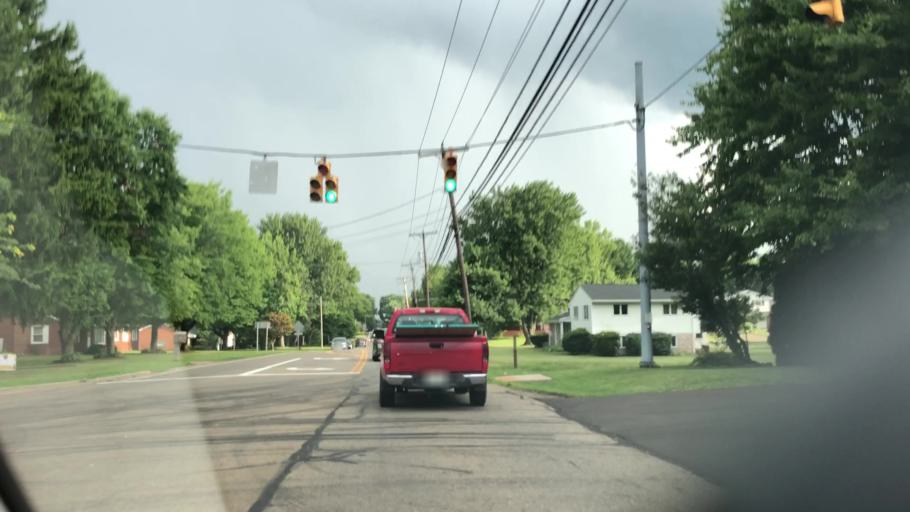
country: US
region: Ohio
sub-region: Stark County
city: North Canton
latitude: 40.8633
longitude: -81.4421
